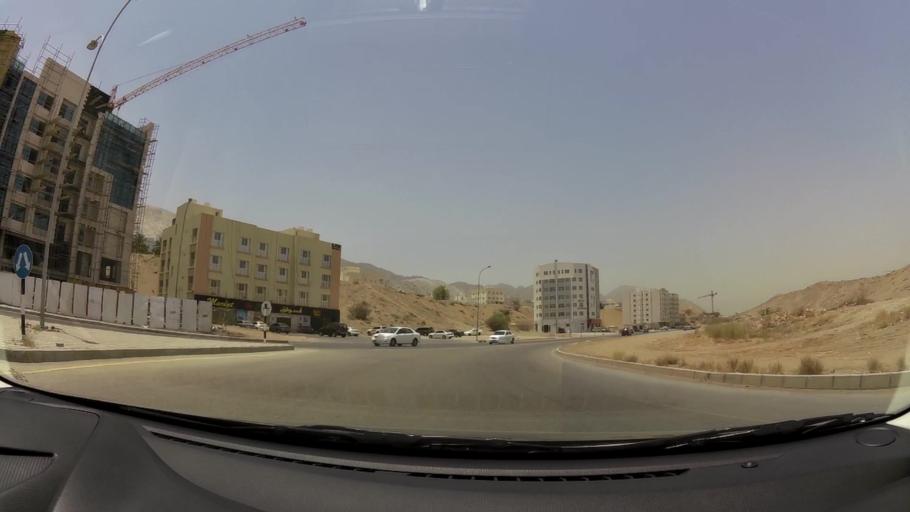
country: OM
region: Muhafazat Masqat
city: Bawshar
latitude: 23.5656
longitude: 58.4130
